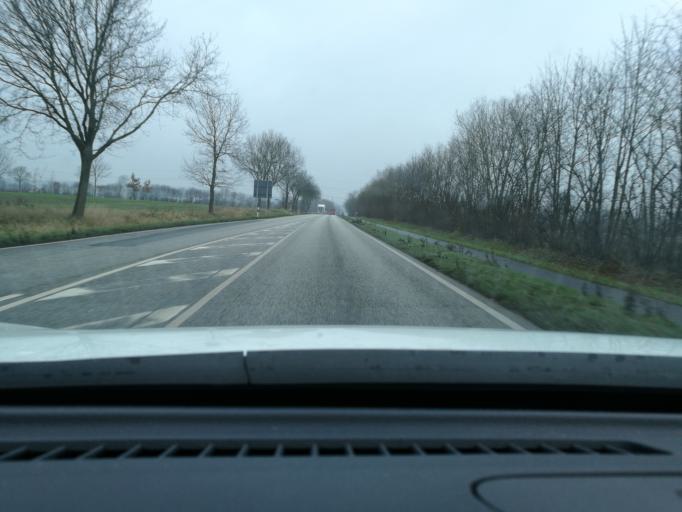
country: DE
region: Schleswig-Holstein
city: Borgstedt
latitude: 54.3369
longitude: 9.6969
